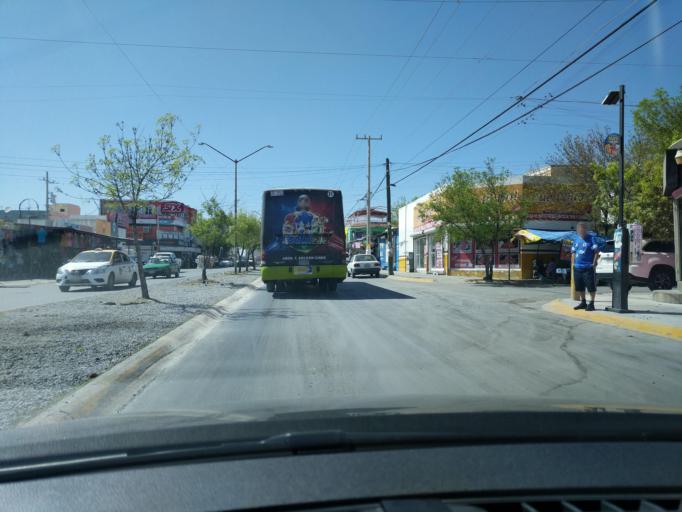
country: MX
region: Nuevo Leon
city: Juarez
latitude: 25.6537
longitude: -100.0785
